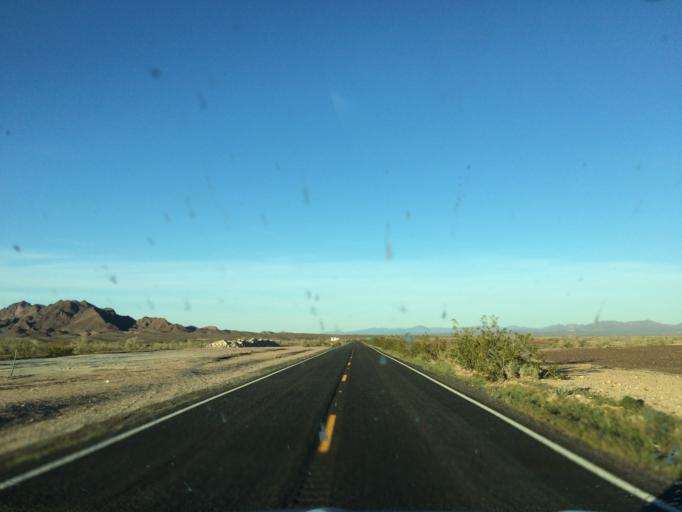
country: US
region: California
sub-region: Riverside County
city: Mesa Verde
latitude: 33.2691
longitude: -114.7973
